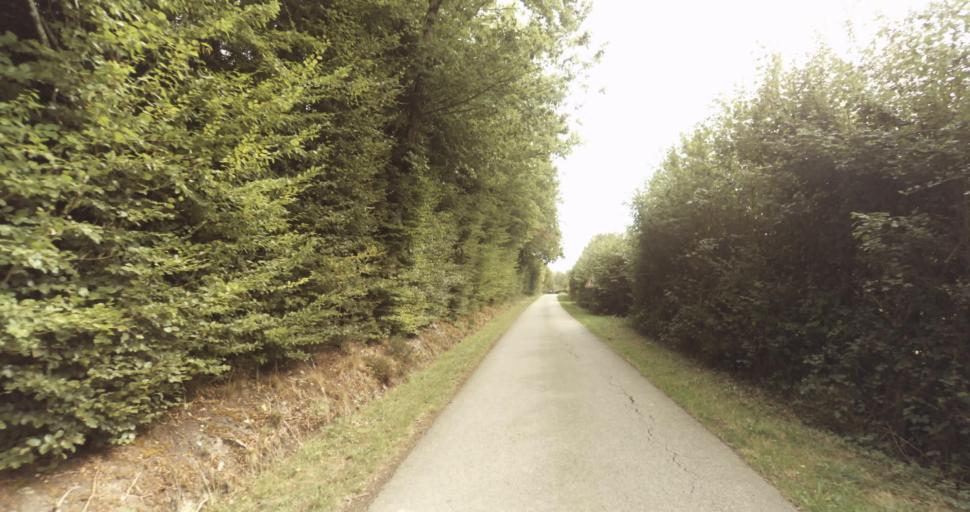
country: FR
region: Lower Normandy
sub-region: Departement de l'Orne
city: Gace
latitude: 48.8271
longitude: 0.3084
